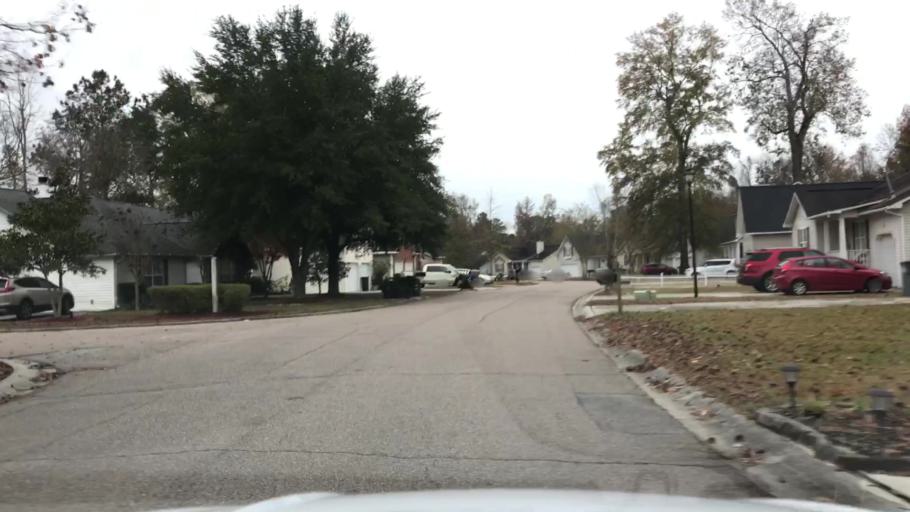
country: US
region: South Carolina
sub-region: Berkeley County
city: Goose Creek
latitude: 32.9680
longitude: -80.0503
